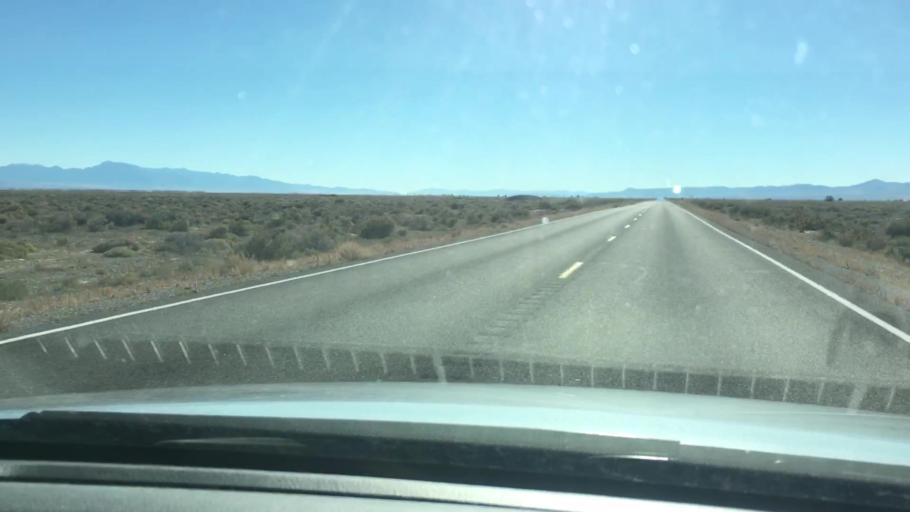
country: US
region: Nevada
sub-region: White Pine County
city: Ely
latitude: 38.6638
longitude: -115.5658
